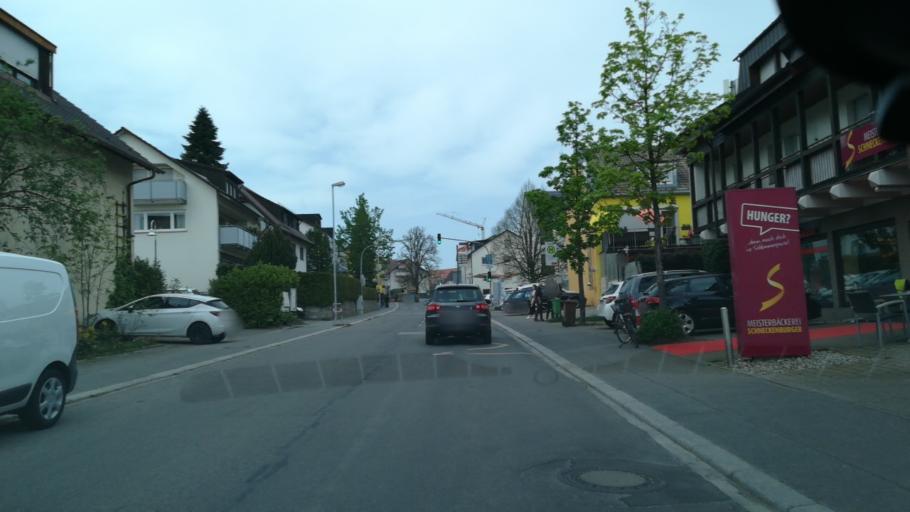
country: DE
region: Baden-Wuerttemberg
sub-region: Freiburg Region
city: Konstanz
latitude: 47.7115
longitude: 9.1731
